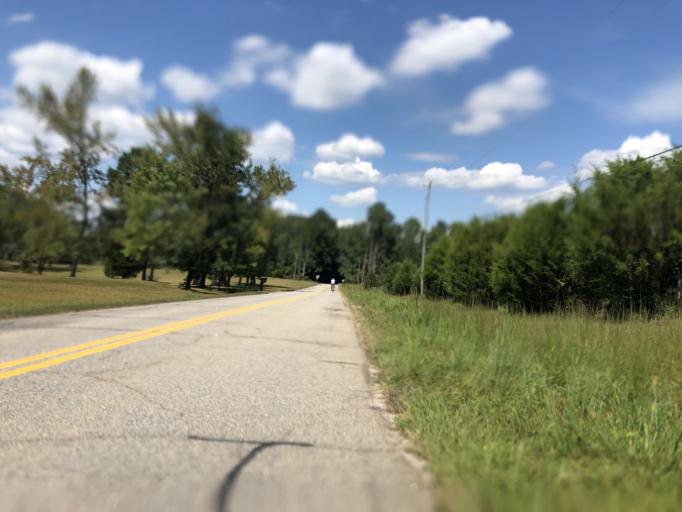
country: US
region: Georgia
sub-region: Fulton County
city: Palmetto
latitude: 33.5091
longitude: -84.6927
